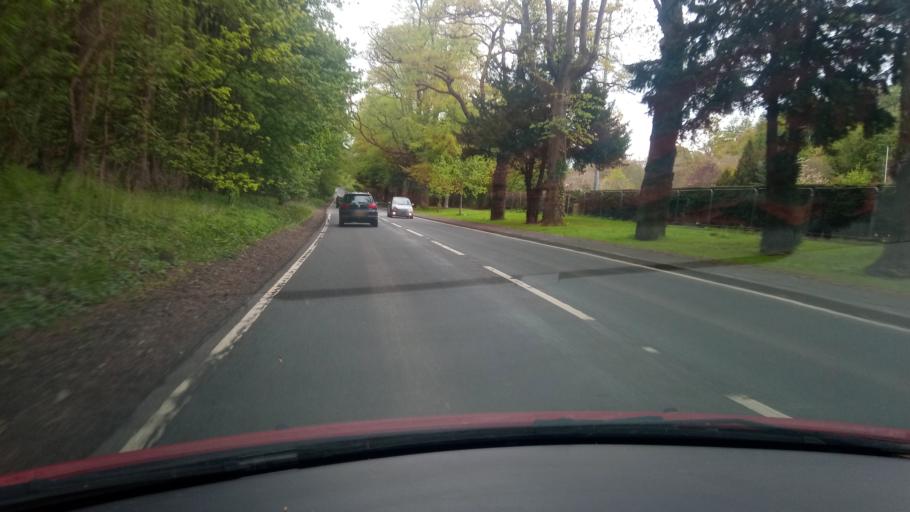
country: GB
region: Scotland
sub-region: The Scottish Borders
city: Jedburgh
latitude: 55.4921
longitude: -2.5449
